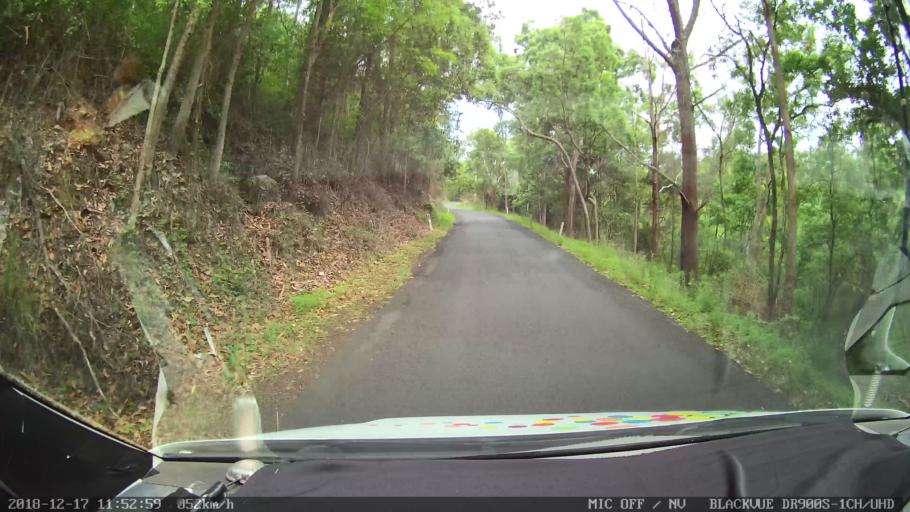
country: AU
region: New South Wales
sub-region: Kyogle
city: Kyogle
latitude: -28.5776
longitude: 152.5876
